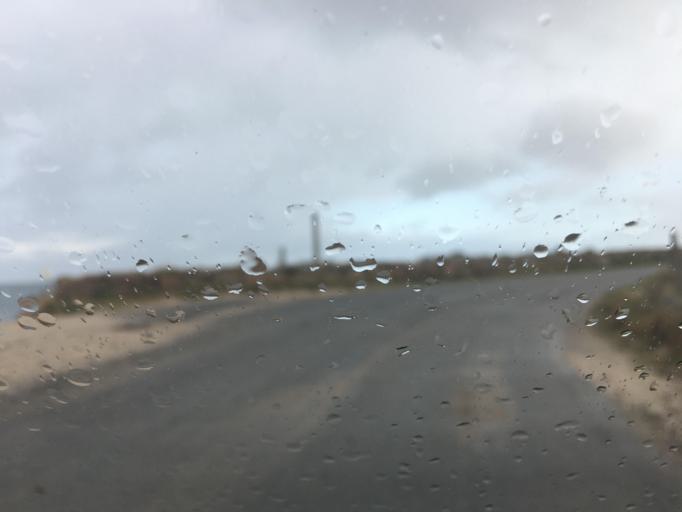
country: FR
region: Lower Normandy
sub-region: Departement de la Manche
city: Reville
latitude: 49.6941
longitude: -1.2761
